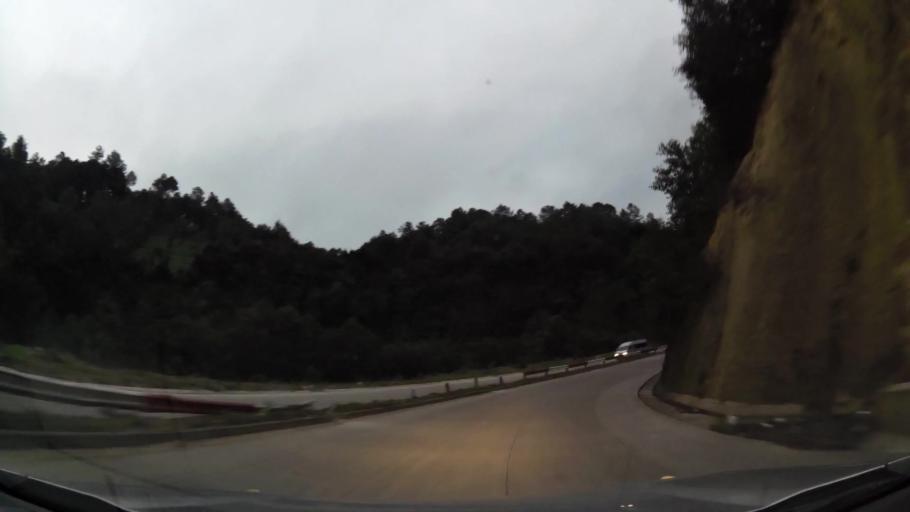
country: GT
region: Chimaltenango
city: Santa Apolonia
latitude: 14.8364
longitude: -91.0420
